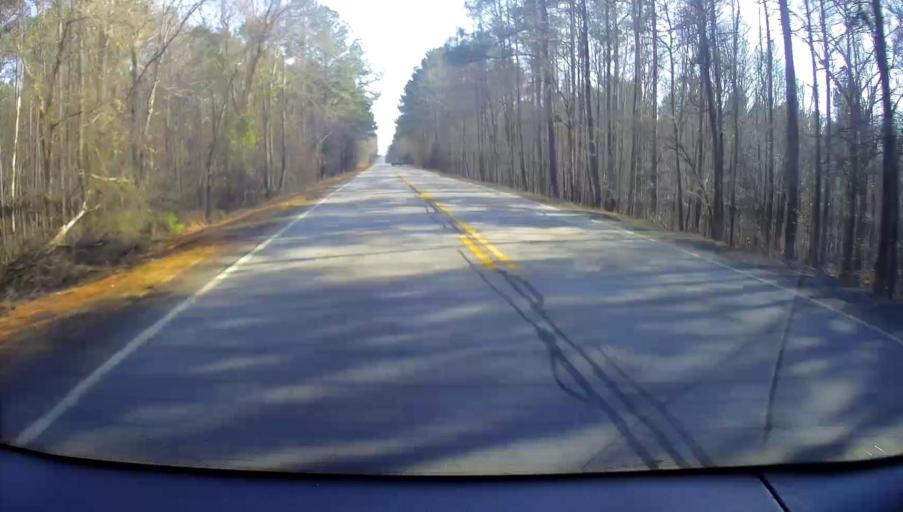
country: US
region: Georgia
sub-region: Butts County
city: Indian Springs
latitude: 33.2080
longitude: -83.8590
